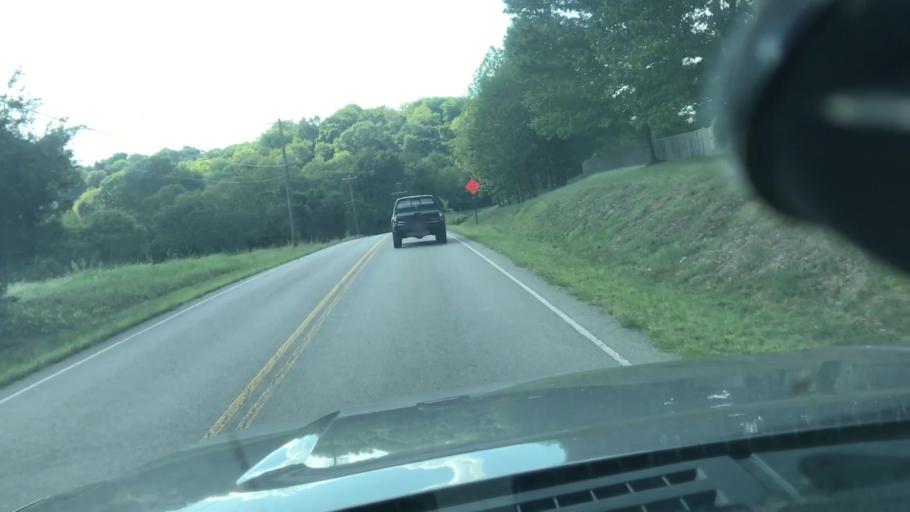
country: US
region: Tennessee
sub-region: Cheatham County
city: Pegram
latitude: 36.0317
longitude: -86.9658
